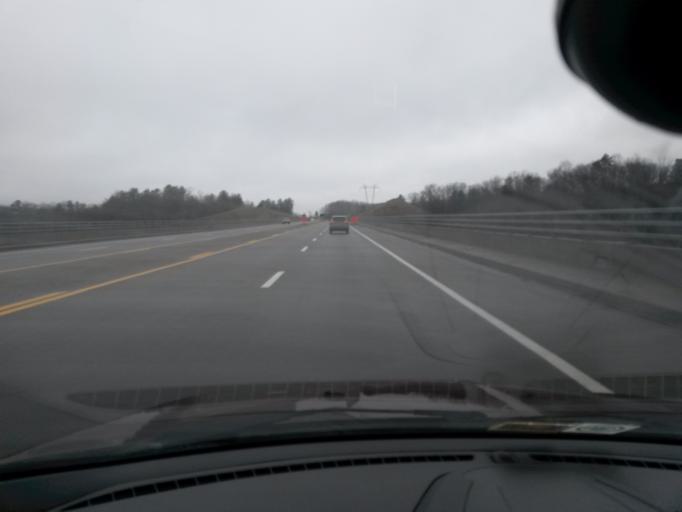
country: US
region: West Virginia
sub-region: Raleigh County
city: Beckley
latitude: 37.7908
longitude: -81.1637
